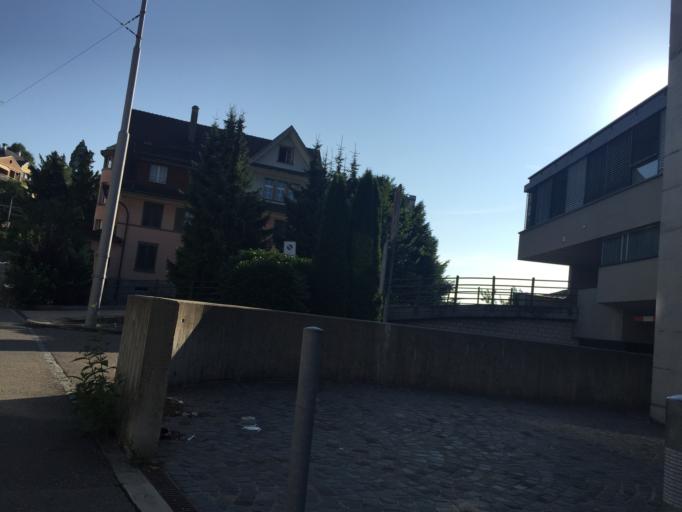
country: CH
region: Saint Gallen
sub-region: Wahlkreis St. Gallen
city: Sankt Gallen
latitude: 47.4283
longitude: 9.3750
